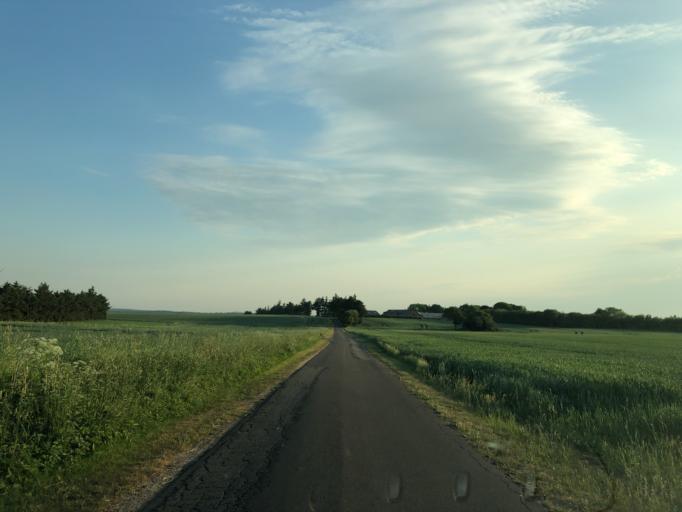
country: DK
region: Central Jutland
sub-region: Holstebro Kommune
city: Holstebro
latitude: 56.3921
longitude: 8.4776
